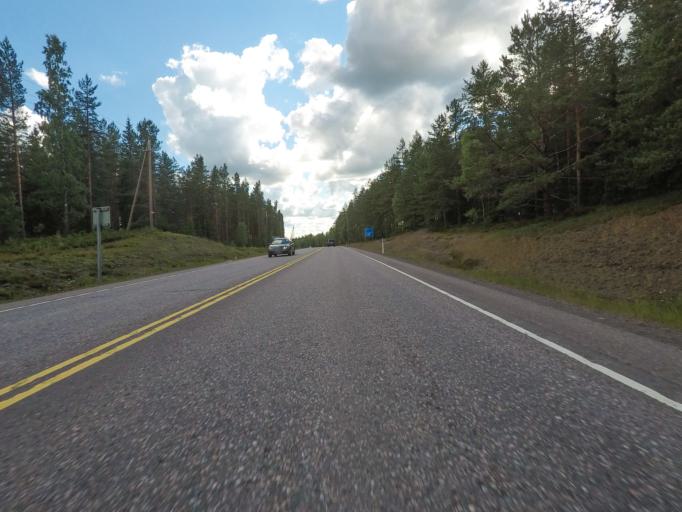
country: FI
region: Uusimaa
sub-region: Helsinki
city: Nurmijaervi
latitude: 60.5106
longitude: 24.6345
